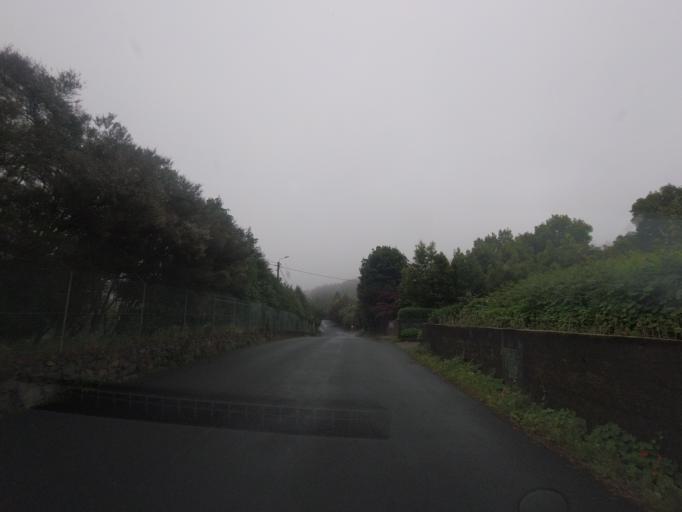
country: PT
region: Madeira
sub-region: Santa Cruz
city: Santa Cruz
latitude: 32.7219
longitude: -16.8113
